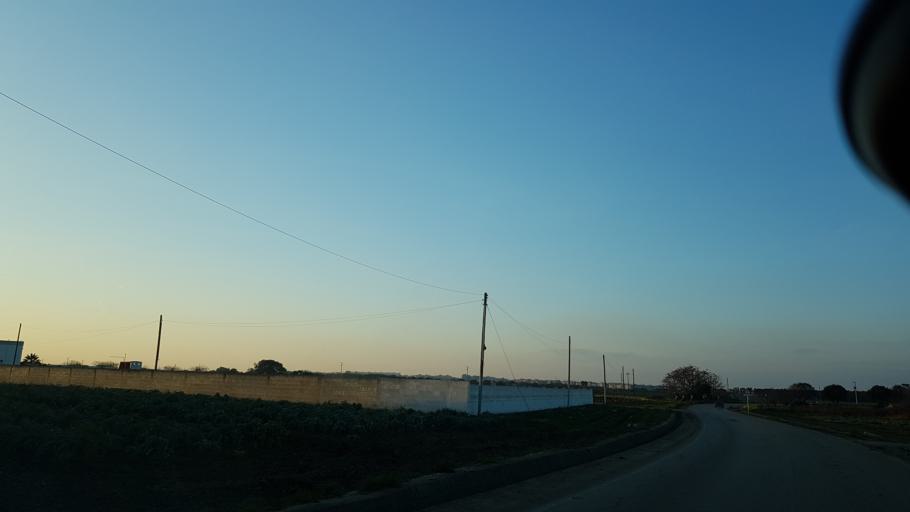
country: IT
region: Apulia
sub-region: Provincia di Brindisi
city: La Rosa
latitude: 40.6044
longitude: 17.9459
